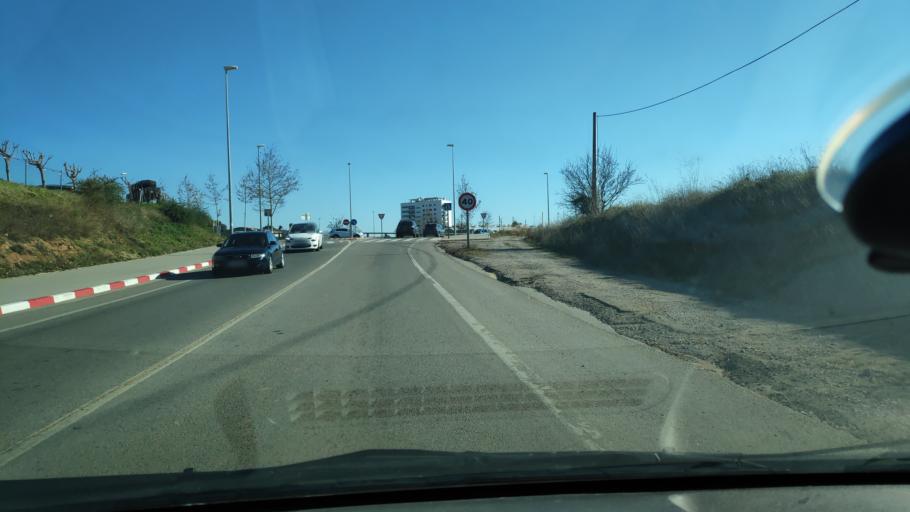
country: ES
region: Catalonia
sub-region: Provincia de Barcelona
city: Sant Quirze del Valles
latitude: 41.5512
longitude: 2.0744
